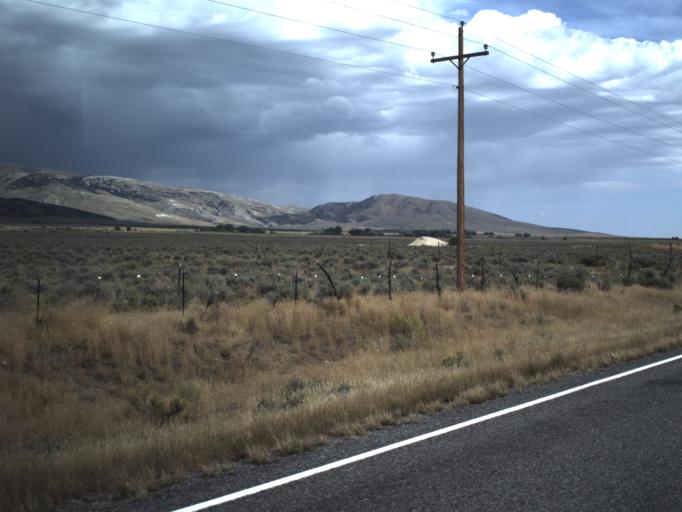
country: US
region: Idaho
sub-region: Cassia County
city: Burley
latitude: 41.8165
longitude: -113.3691
